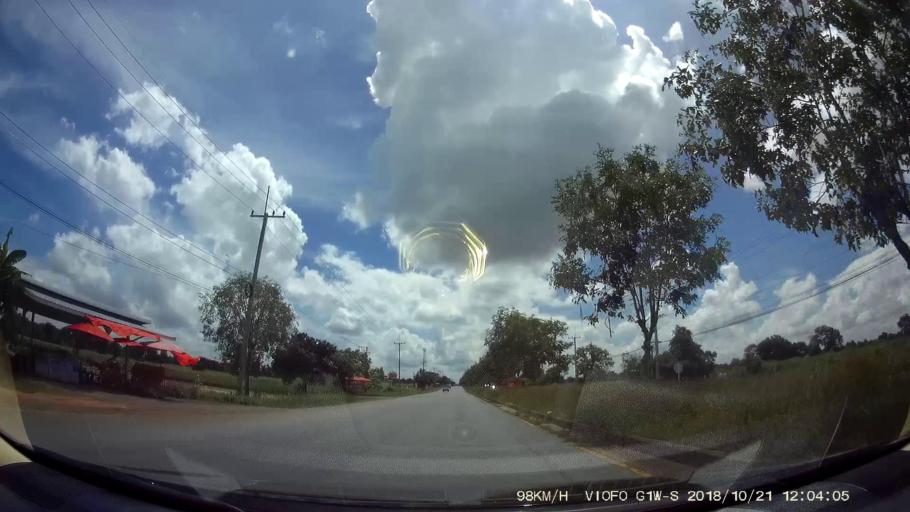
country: TH
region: Chaiyaphum
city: Chatturat
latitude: 15.4997
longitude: 101.8204
